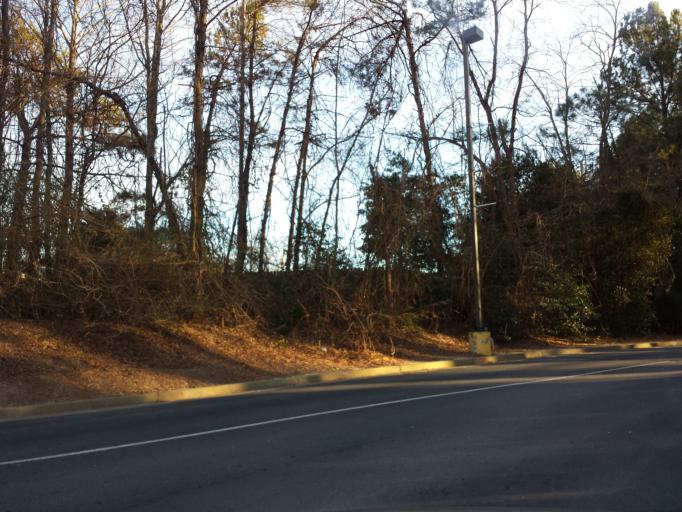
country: US
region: Georgia
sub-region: Fulton County
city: Roswell
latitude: 33.9840
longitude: -84.4293
